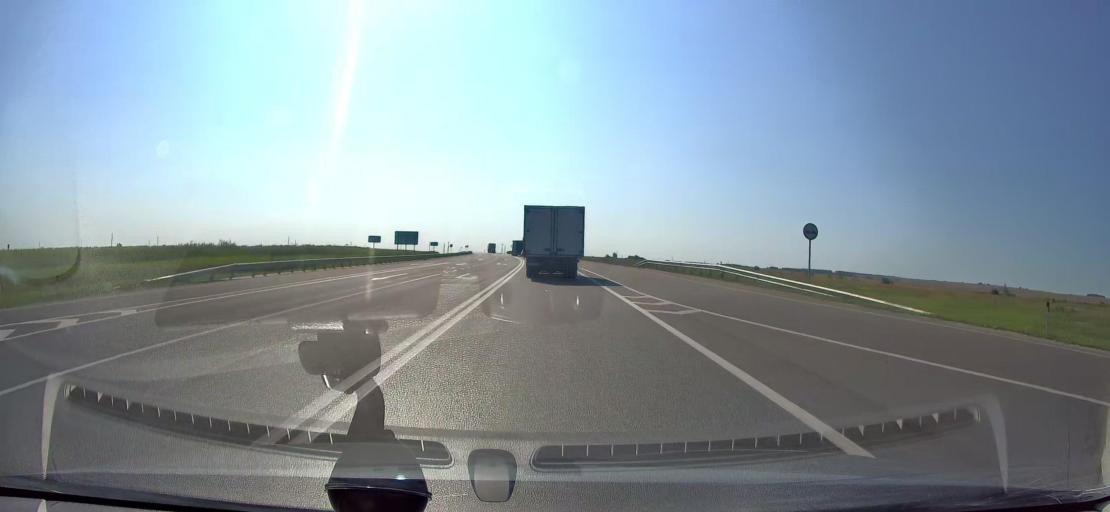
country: RU
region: Orjol
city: Kromy
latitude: 52.6556
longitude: 35.7193
